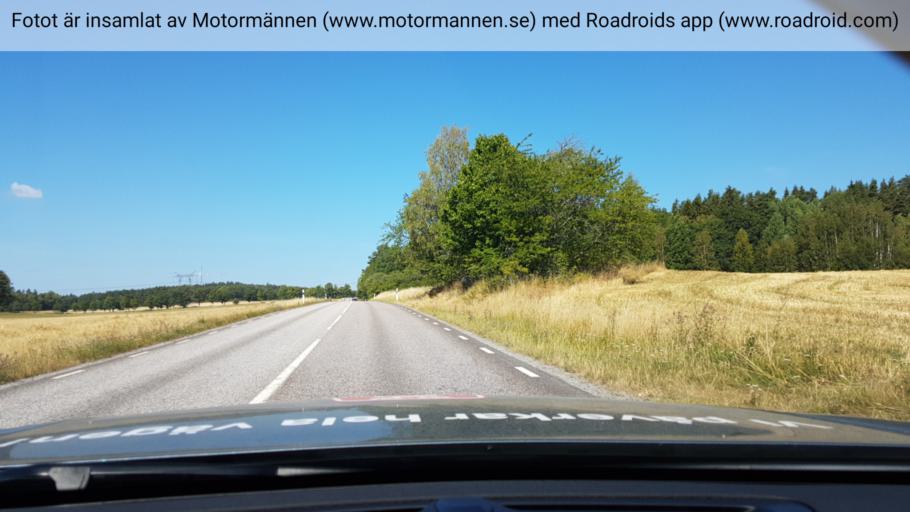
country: SE
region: Stockholm
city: Stenhamra
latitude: 59.2971
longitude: 17.6680
